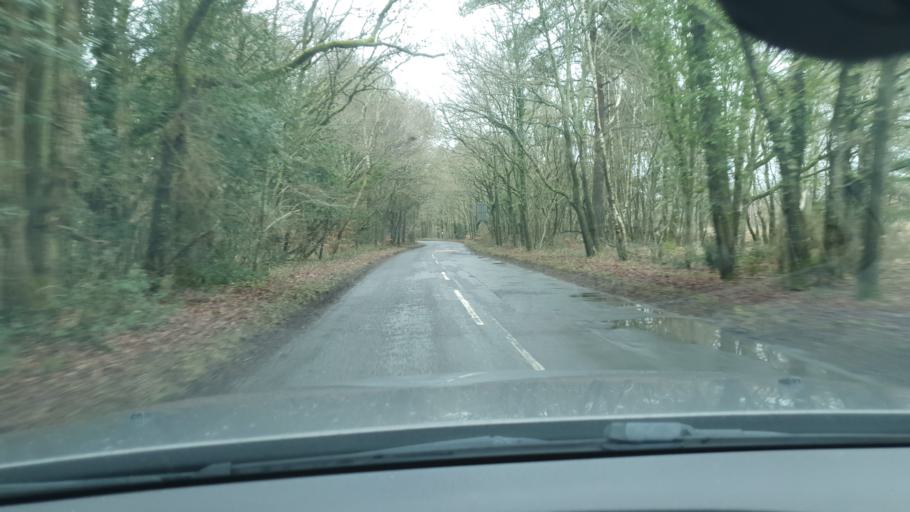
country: GB
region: England
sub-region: West Berkshire
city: Greenham
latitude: 51.3618
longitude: -1.3201
